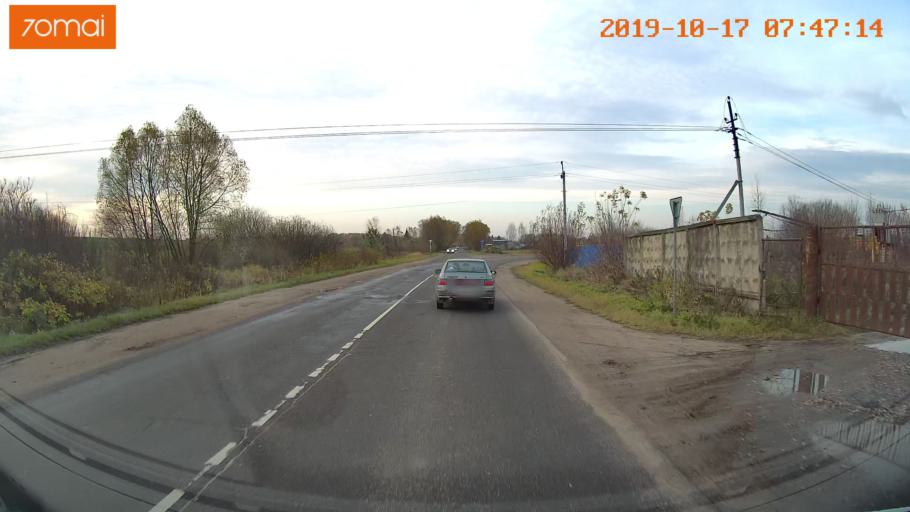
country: RU
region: Vladimir
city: Yur'yev-Pol'skiy
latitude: 56.4887
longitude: 39.6868
